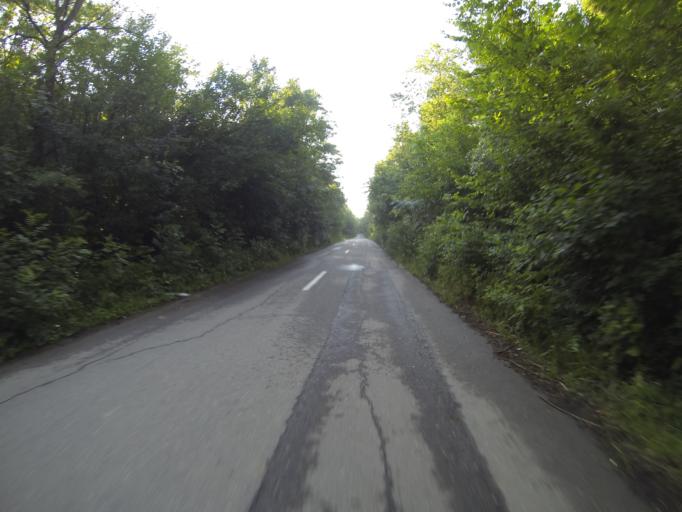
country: RO
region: Dolj
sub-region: Comuna Tuglui
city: Tuglui
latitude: 44.1732
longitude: 23.8189
